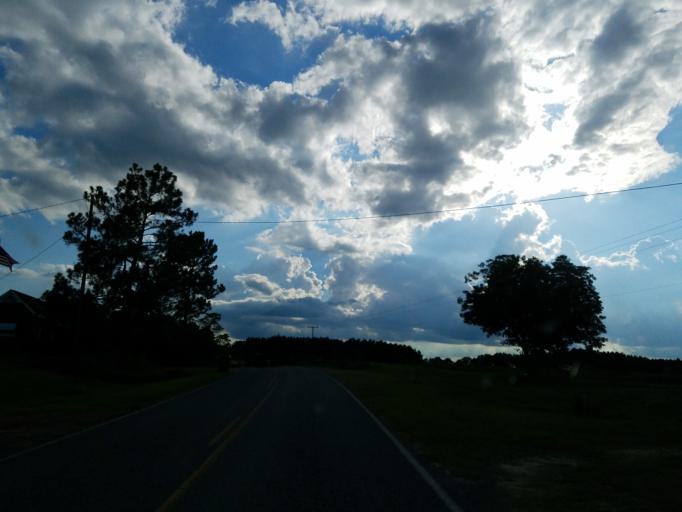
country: US
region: Georgia
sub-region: Turner County
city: Ashburn
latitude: 31.6211
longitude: -83.5987
